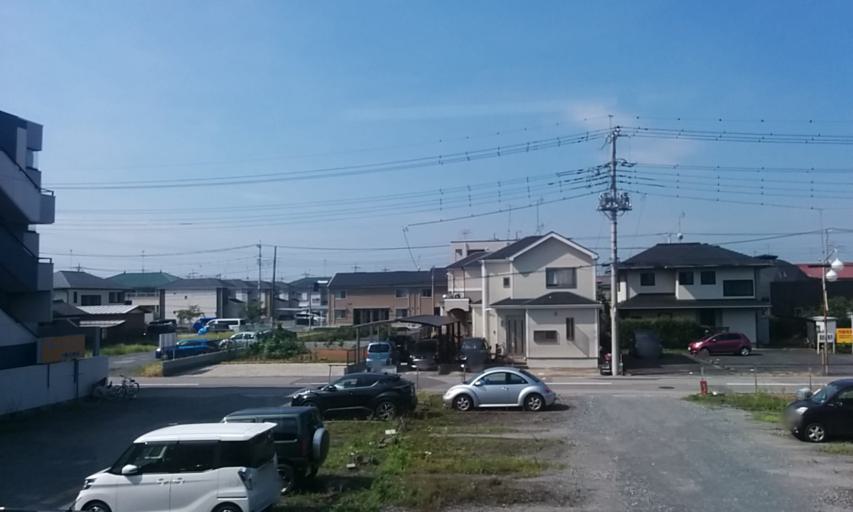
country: JP
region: Saitama
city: Kazo
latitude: 36.1093
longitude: 139.6351
